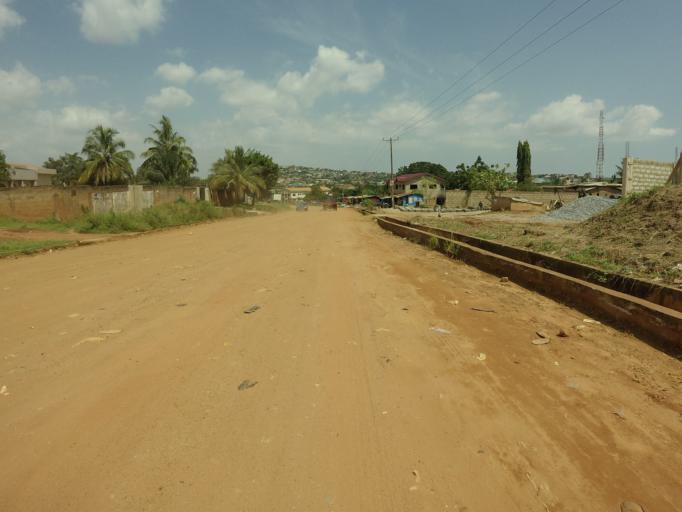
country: GH
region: Greater Accra
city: Gbawe
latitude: 5.6195
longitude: -0.3082
